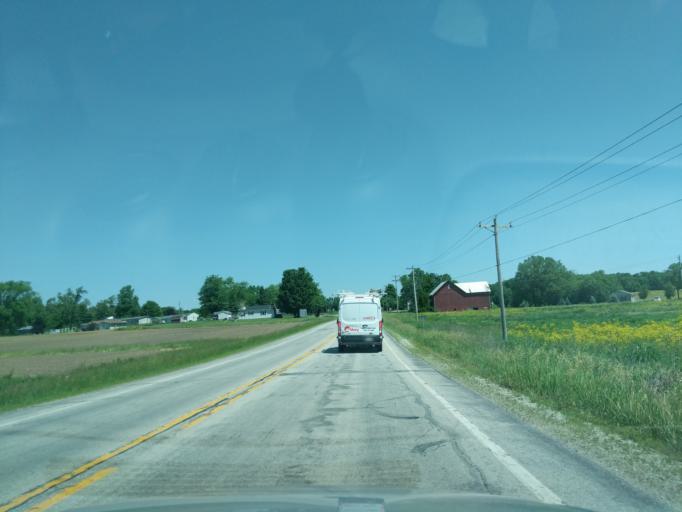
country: US
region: Indiana
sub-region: Whitley County
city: Columbia City
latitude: 41.1908
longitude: -85.4915
